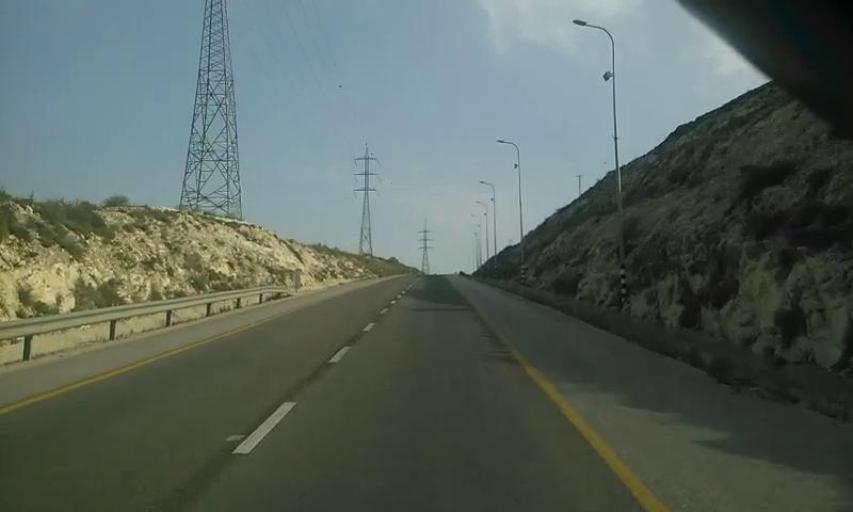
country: PS
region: West Bank
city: Sarrah
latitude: 32.2080
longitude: 35.1827
